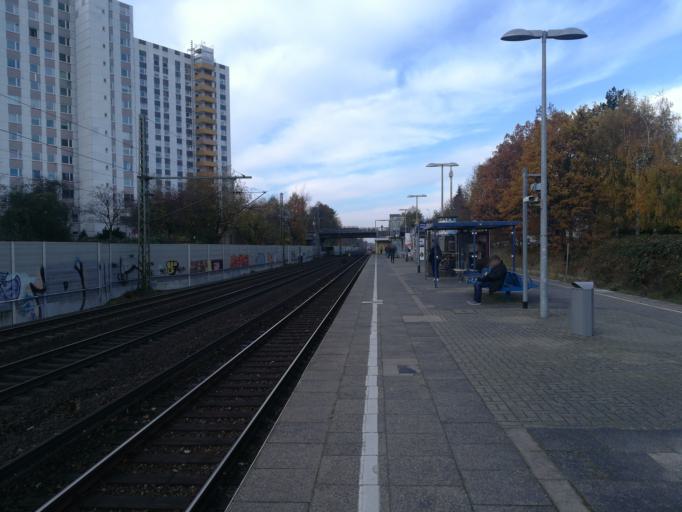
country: DE
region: Schleswig-Holstein
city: Rellingen
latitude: 53.6436
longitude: 9.8150
